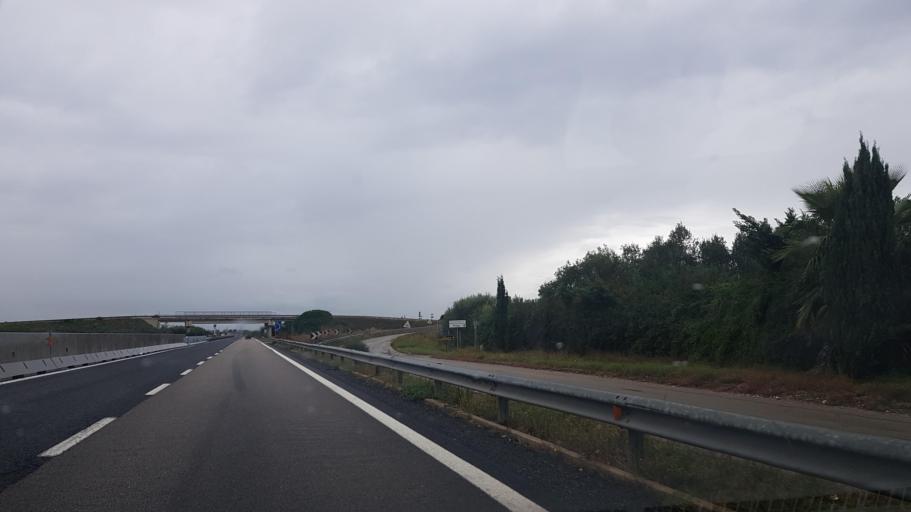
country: IT
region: Apulia
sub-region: Provincia di Taranto
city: Massafra
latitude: 40.5307
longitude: 17.0875
